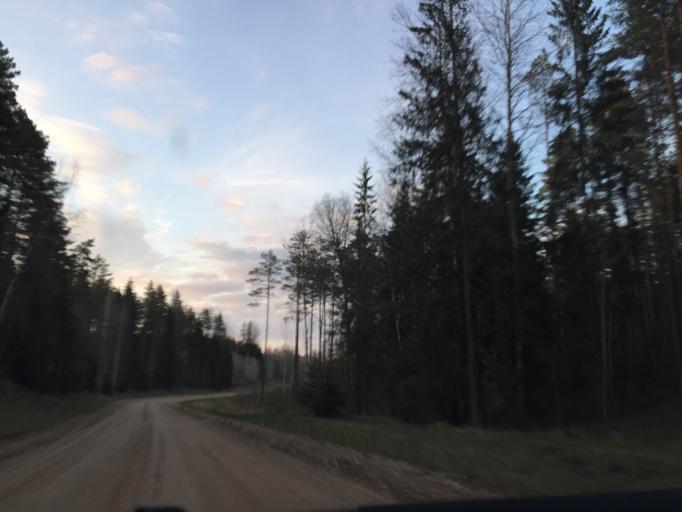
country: LV
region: Aluksnes Rajons
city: Aluksne
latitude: 57.3090
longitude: 26.9141
